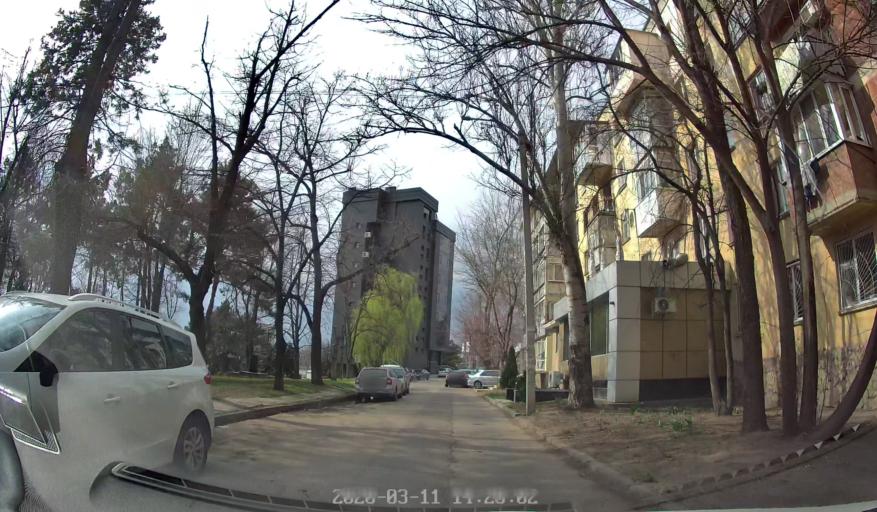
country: MD
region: Chisinau
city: Chisinau
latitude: 47.0385
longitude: 28.8602
